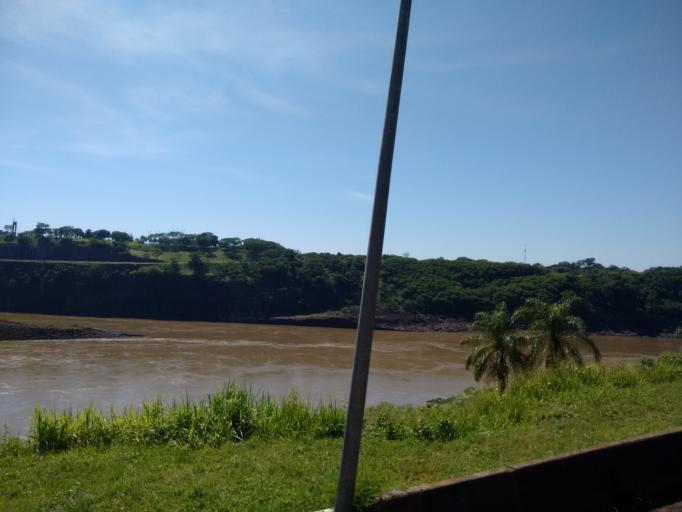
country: PY
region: Alto Parana
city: Ciudad del Este
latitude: -25.4126
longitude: -54.5938
